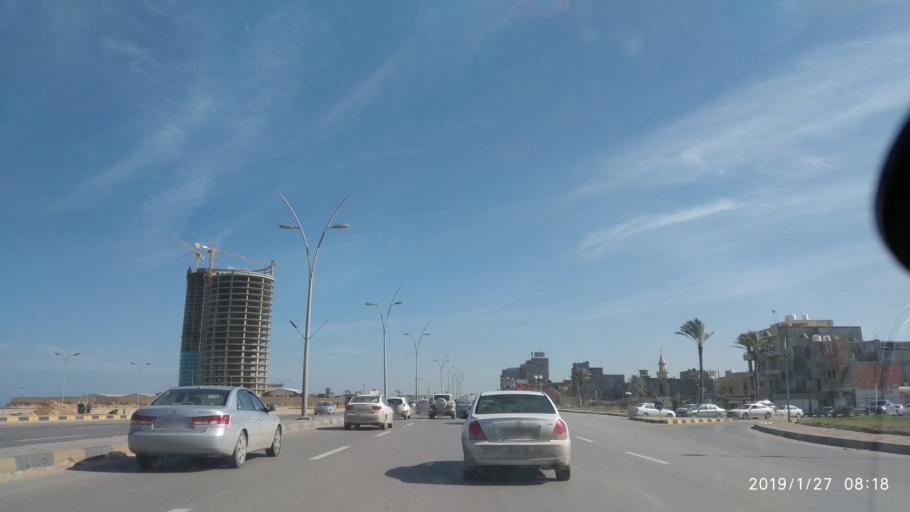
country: LY
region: Tripoli
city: Tripoli
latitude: 32.9066
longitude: 13.2609
